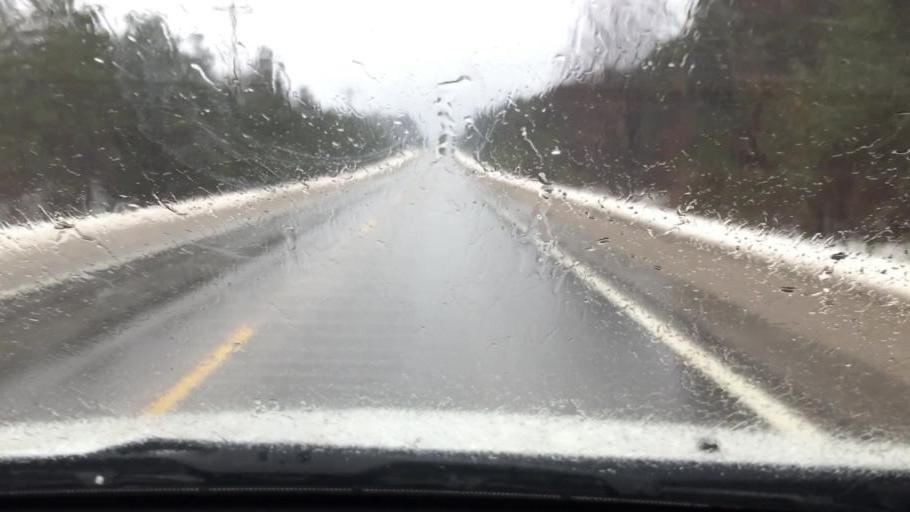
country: US
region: Michigan
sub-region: Charlevoix County
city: Charlevoix
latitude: 45.2690
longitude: -85.2083
